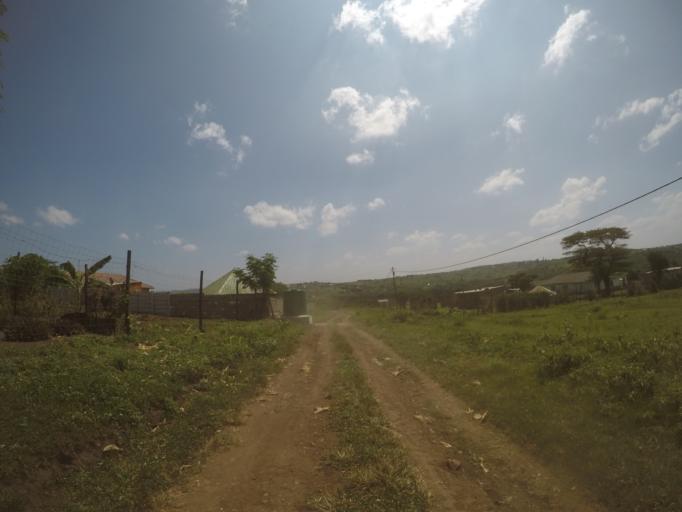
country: ZA
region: KwaZulu-Natal
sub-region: uThungulu District Municipality
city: Empangeni
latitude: -28.5922
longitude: 31.7379
